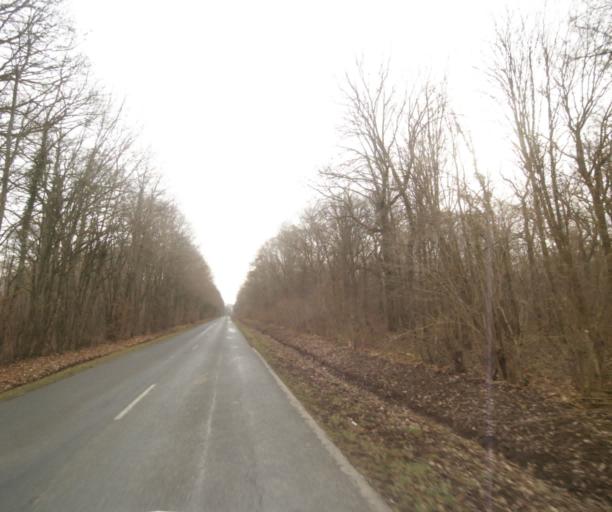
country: FR
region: Champagne-Ardenne
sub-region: Departement de la Haute-Marne
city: Villiers-en-Lieu
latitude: 48.7126
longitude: 4.8856
